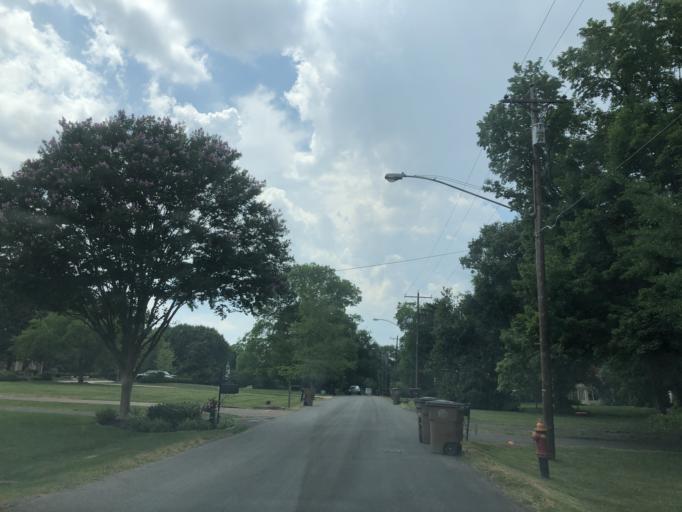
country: US
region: Tennessee
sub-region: Davidson County
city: Belle Meade
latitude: 36.1170
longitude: -86.8200
